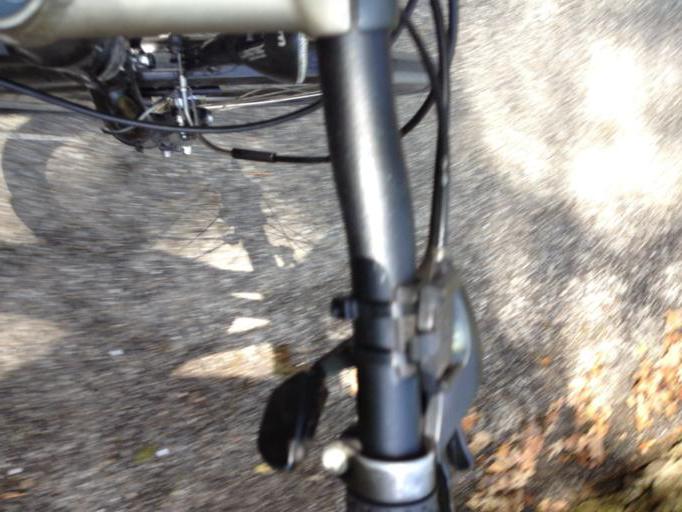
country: FR
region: Rhone-Alpes
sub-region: Departement de la Savoie
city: La Motte-Servolex
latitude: 45.5817
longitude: 5.8351
